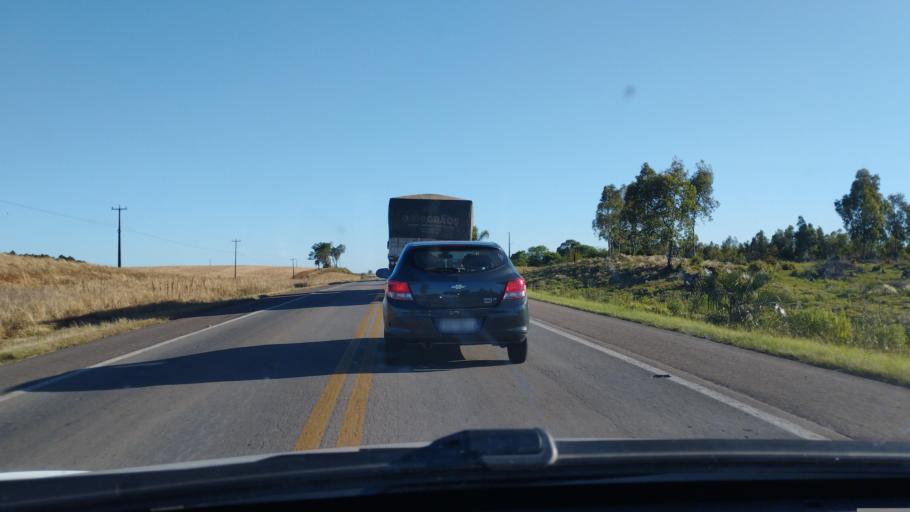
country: BR
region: Rio Grande do Sul
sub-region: Julio De Castilhos
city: Julio de Castilhos
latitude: -29.3786
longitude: -53.6705
